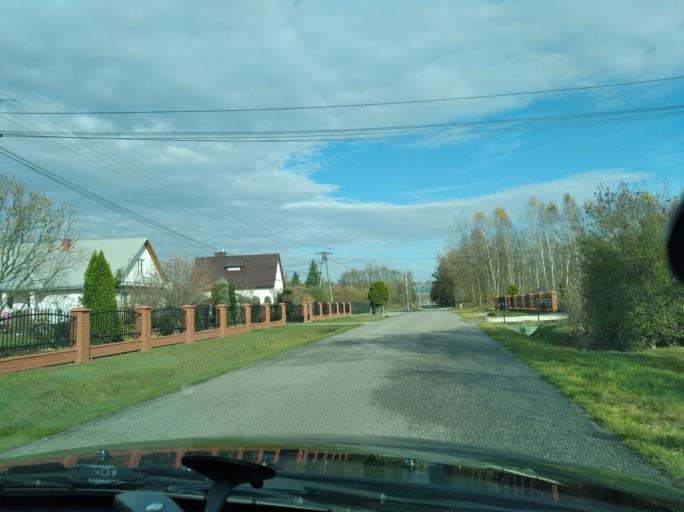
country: PL
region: Subcarpathian Voivodeship
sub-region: Powiat ropczycko-sedziszowski
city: Sedziszow Malopolski
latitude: 50.1067
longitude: 21.6846
